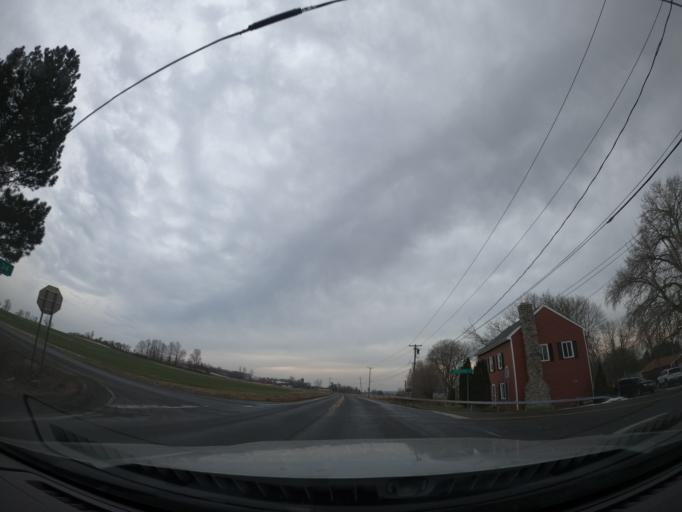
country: US
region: New York
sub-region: Cayuga County
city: Melrose Park
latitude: 42.7647
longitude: -76.5577
